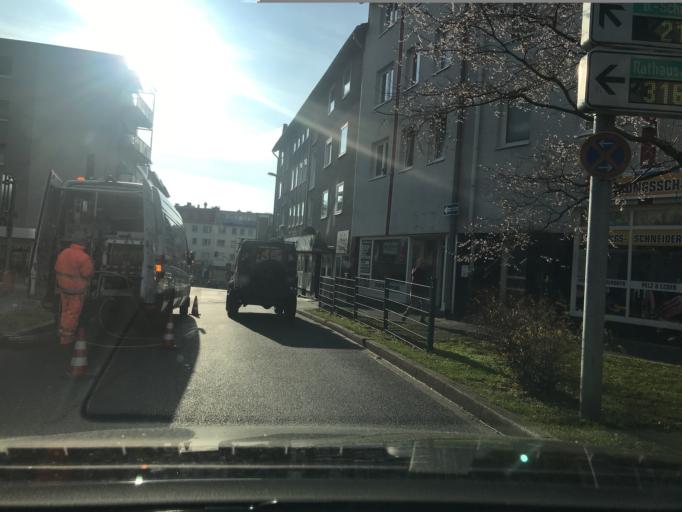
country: DE
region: North Rhine-Westphalia
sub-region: Regierungsbezirk Dusseldorf
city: Remscheid
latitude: 51.1825
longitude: 7.1843
